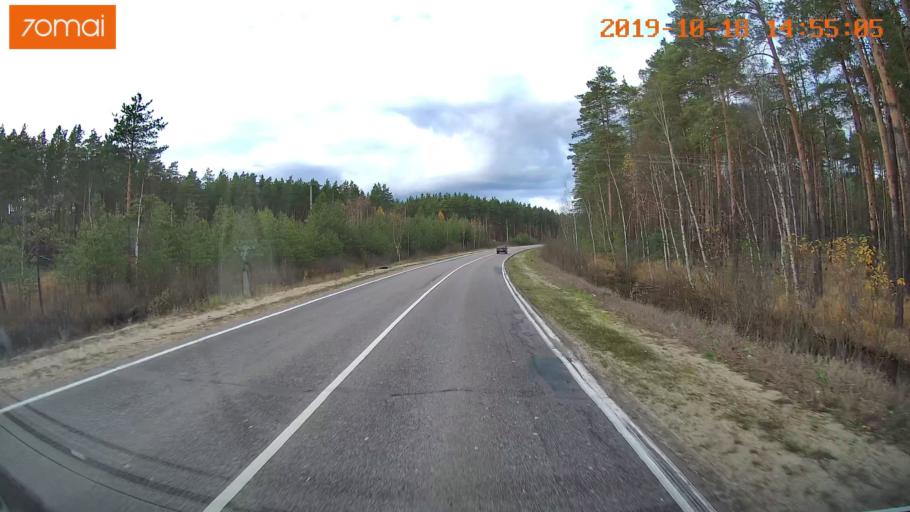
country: RU
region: Vladimir
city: Kurlovo
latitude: 55.4471
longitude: 40.5894
